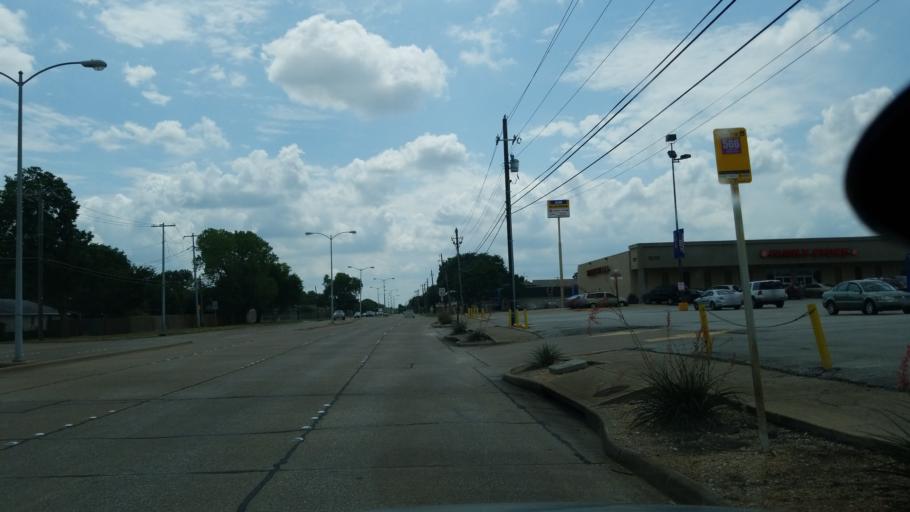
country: US
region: Texas
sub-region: Dallas County
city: Garland
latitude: 32.9301
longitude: -96.6483
